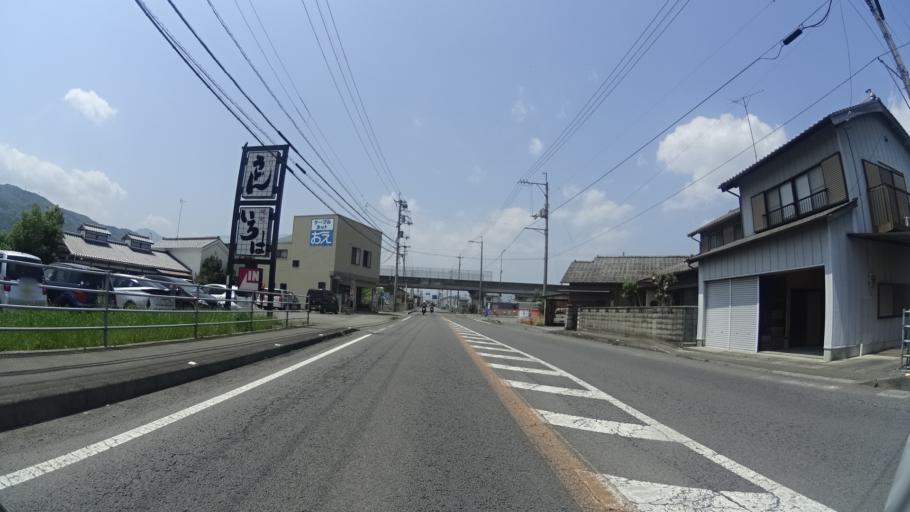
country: JP
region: Tokushima
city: Kamojimacho-jogejima
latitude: 34.0634
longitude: 134.2820
